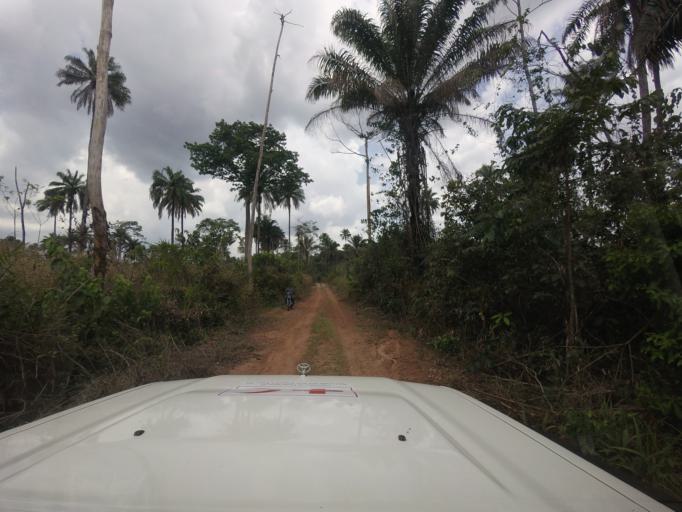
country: LR
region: Lofa
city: Voinjama
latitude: 8.3921
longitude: -9.6244
